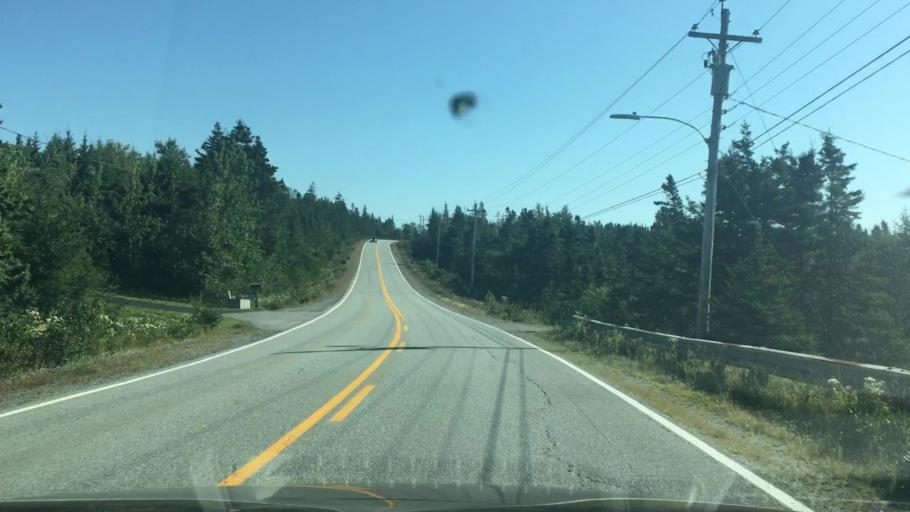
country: CA
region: Nova Scotia
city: Cole Harbour
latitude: 44.7776
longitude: -62.7852
